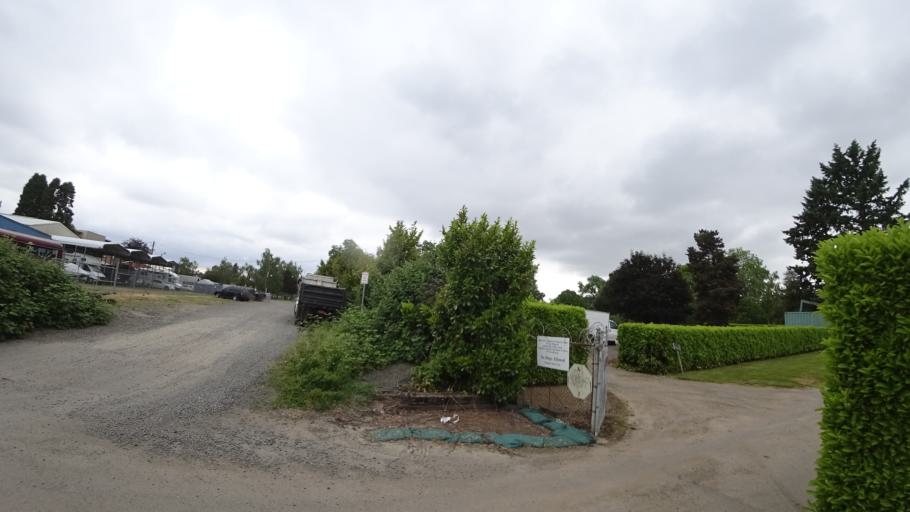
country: US
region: Oregon
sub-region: Multnomah County
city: Portland
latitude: 45.5493
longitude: -122.6102
